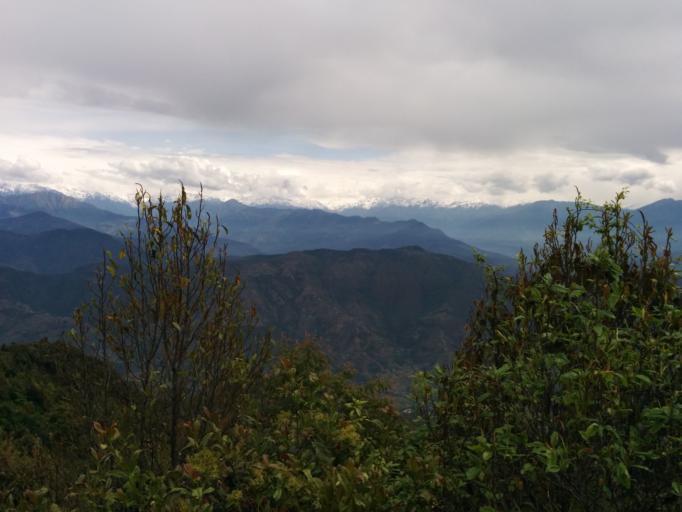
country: NP
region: Central Region
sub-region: Bagmati Zone
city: Nagarkot
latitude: 27.7858
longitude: 85.4805
